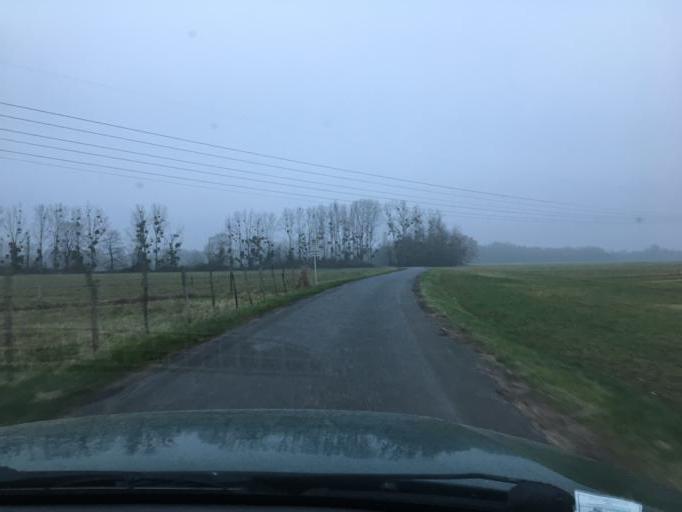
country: FR
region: Centre
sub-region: Departement du Loiret
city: Lailly-en-Val
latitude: 47.7667
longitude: 1.6622
